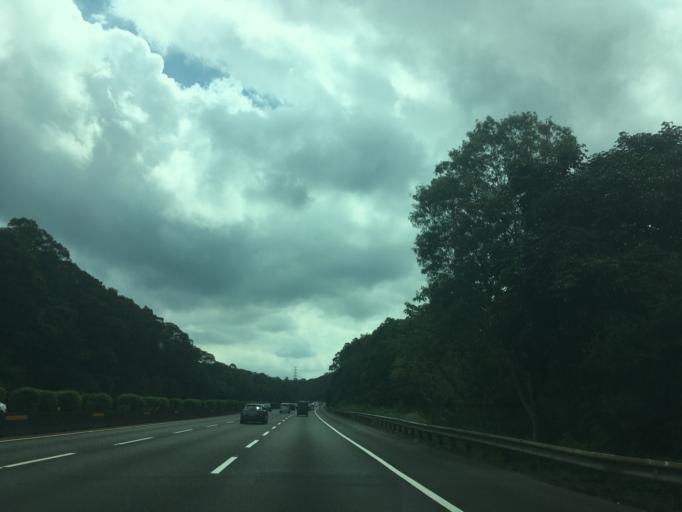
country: TW
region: Taiwan
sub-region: Hsinchu
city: Zhubei
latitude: 24.7786
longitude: 121.1033
